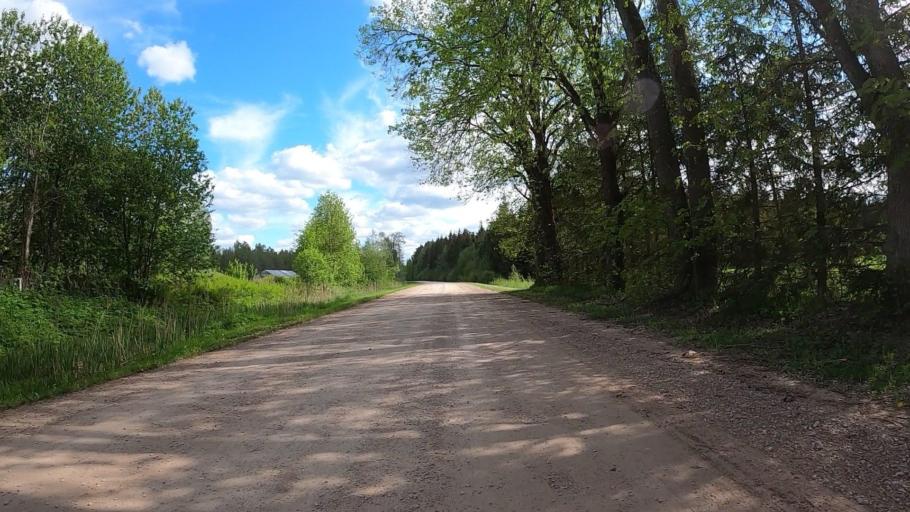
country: LV
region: Jurmala
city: Jurmala
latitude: 56.8652
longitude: 23.7875
